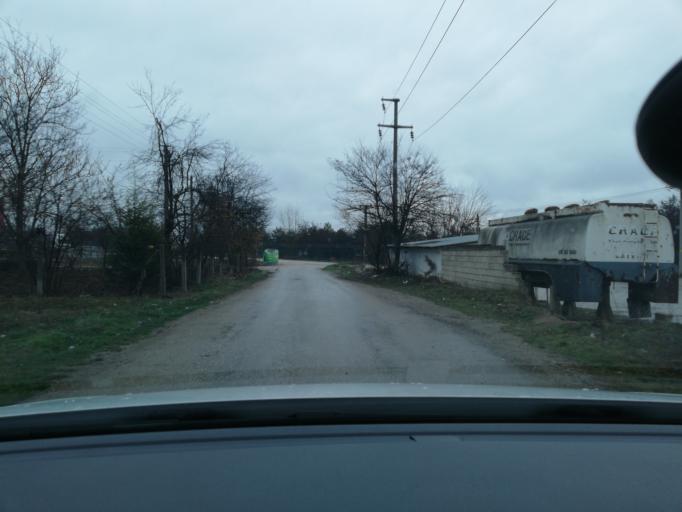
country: TR
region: Bolu
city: Bolu
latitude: 40.7634
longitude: 31.6393
